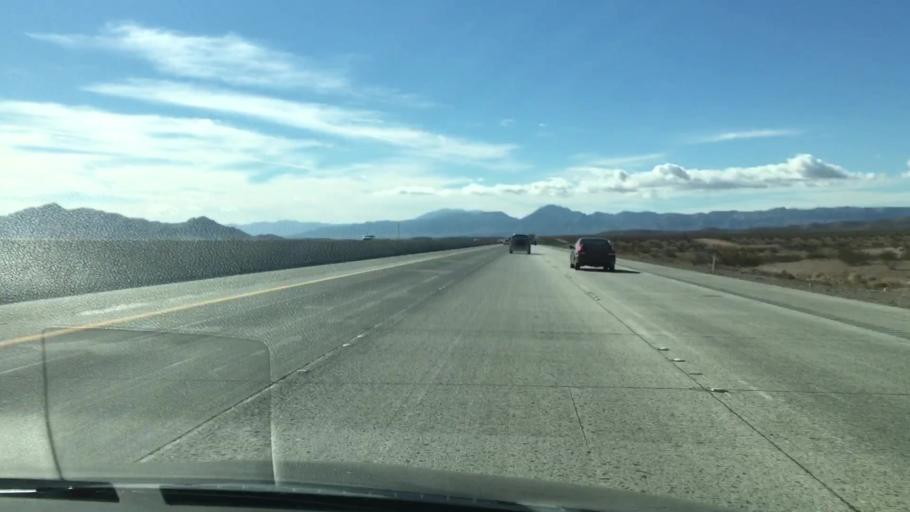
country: US
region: Nevada
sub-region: Clark County
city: Enterprise
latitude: 35.8525
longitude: -115.2645
